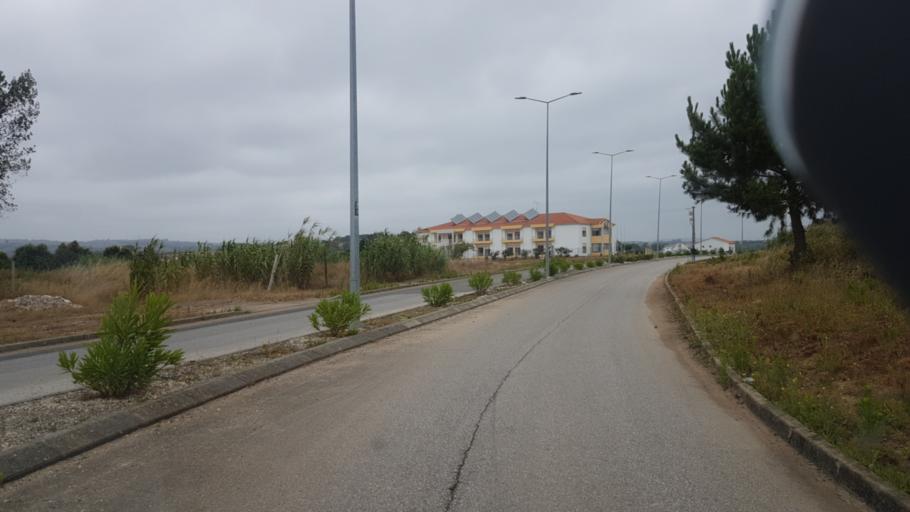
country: PT
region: Leiria
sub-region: Bombarral
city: Bombarral
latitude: 39.2736
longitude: -9.1653
